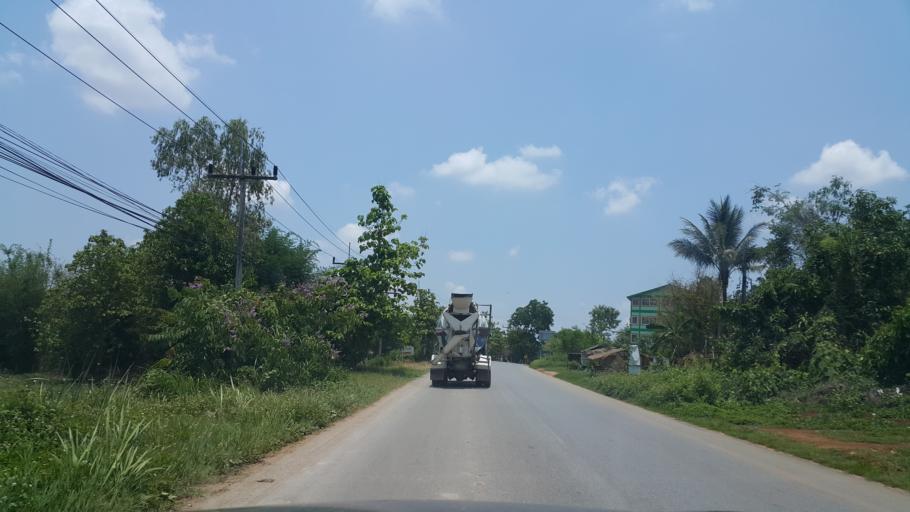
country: TH
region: Chiang Rai
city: Chiang Rai
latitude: 19.9369
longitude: 99.8105
